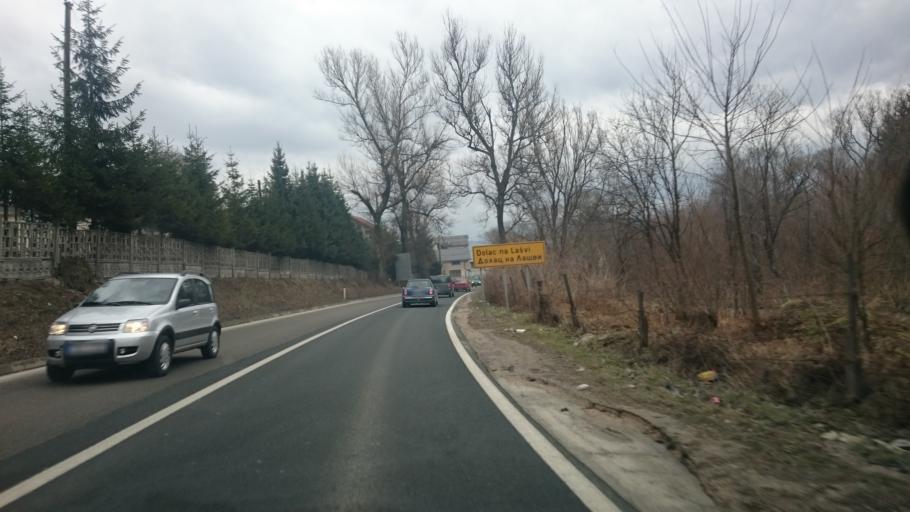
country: BA
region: Federation of Bosnia and Herzegovina
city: Travnik
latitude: 44.2224
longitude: 17.6905
